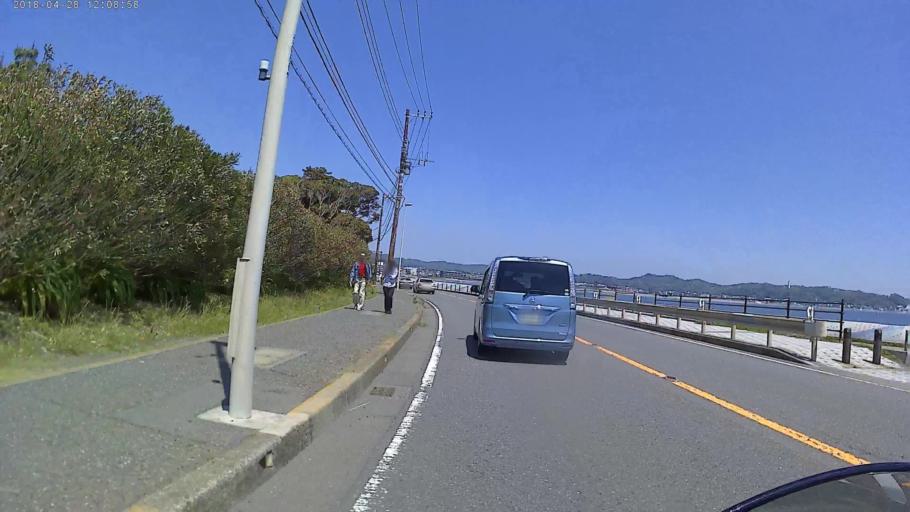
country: JP
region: Kanagawa
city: Kamakura
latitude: 35.3041
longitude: 139.5315
